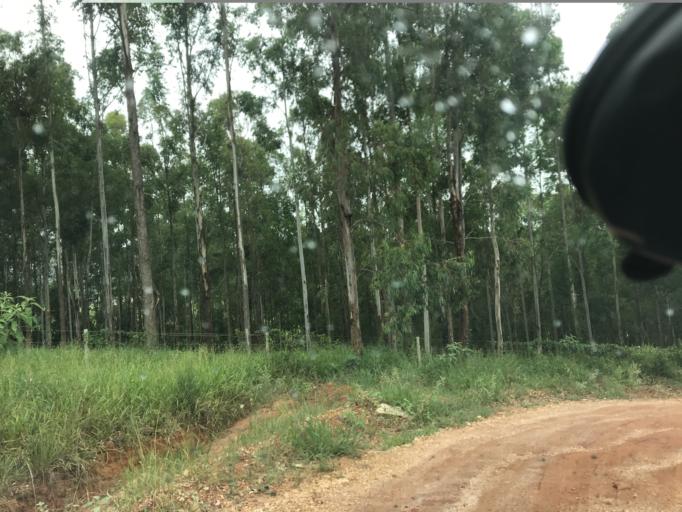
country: BR
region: Minas Gerais
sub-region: Conceicao Do Rio Verde
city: Conceicao do Rio Verde
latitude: -21.6981
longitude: -45.0007
